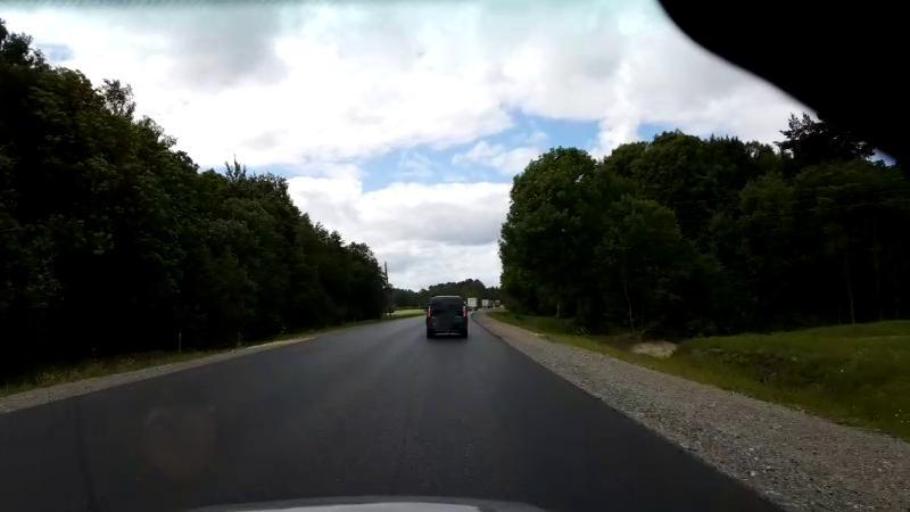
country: LV
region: Salacgrivas
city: Ainazi
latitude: 57.8511
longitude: 24.3570
